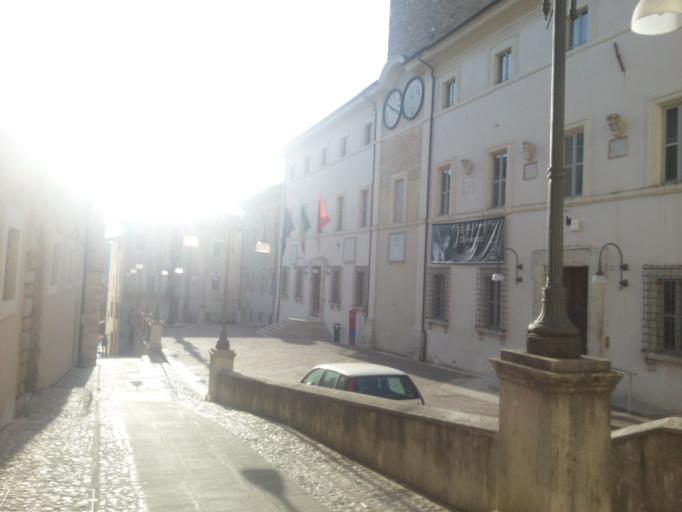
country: IT
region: Umbria
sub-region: Provincia di Perugia
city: Spoleto
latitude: 42.7342
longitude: 12.7386
